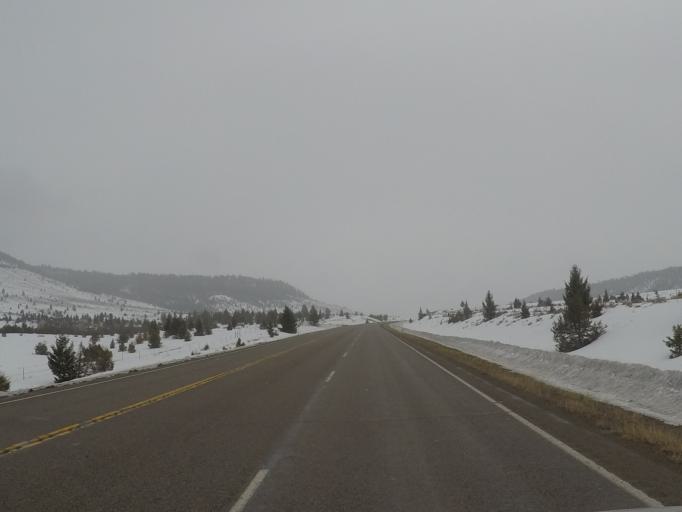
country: US
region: Montana
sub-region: Meagher County
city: White Sulphur Springs
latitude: 46.6652
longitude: -110.8760
